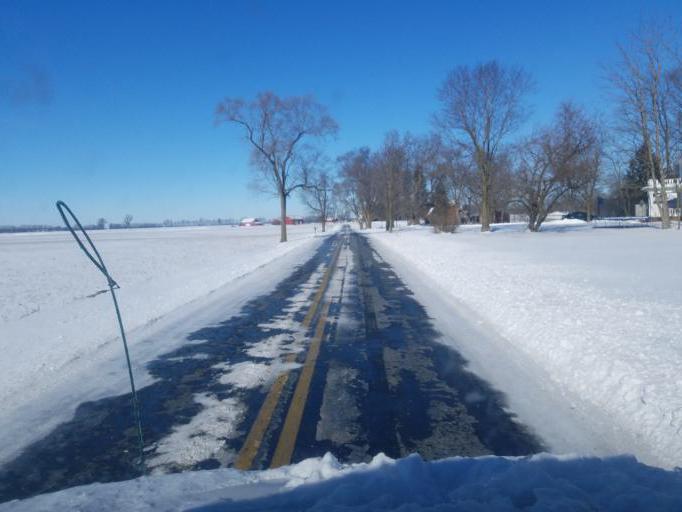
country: US
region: Ohio
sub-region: Delaware County
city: Delaware
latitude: 40.2958
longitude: -82.9867
